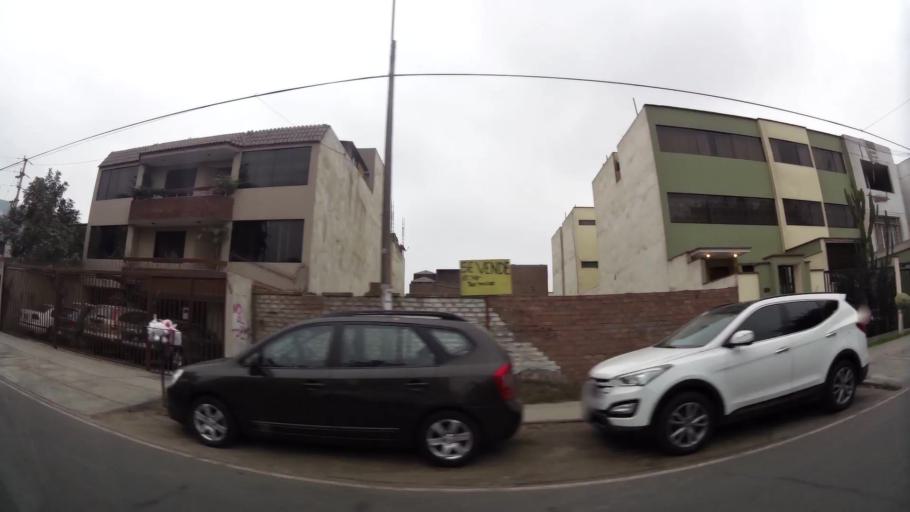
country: PE
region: Lima
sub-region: Lima
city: La Molina
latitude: -12.0975
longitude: -76.9463
